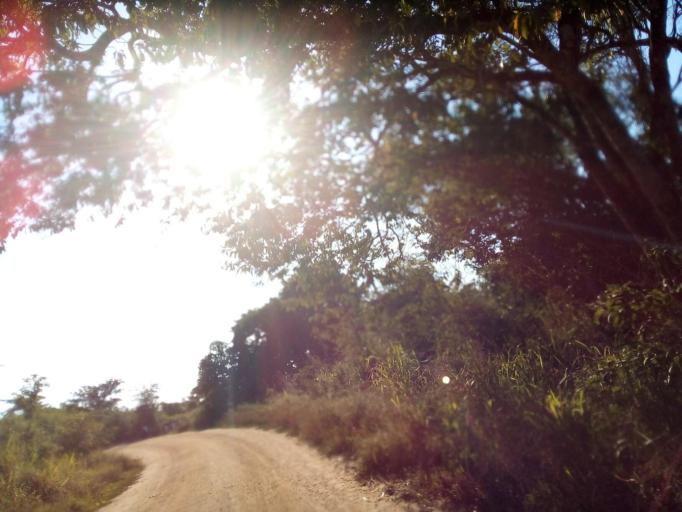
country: MZ
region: Zambezia
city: Quelimane
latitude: -17.4783
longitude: 36.5415
